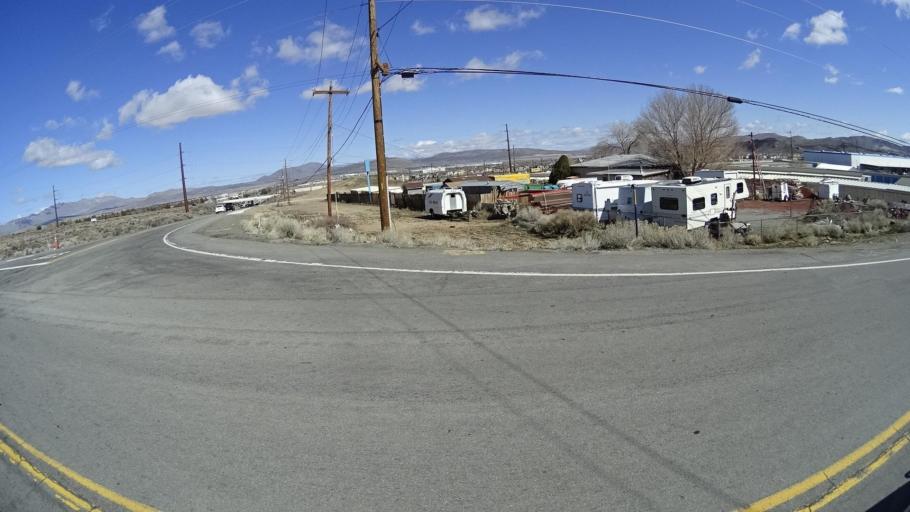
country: US
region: Nevada
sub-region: Washoe County
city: Lemmon Valley
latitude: 39.6144
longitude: -119.8804
